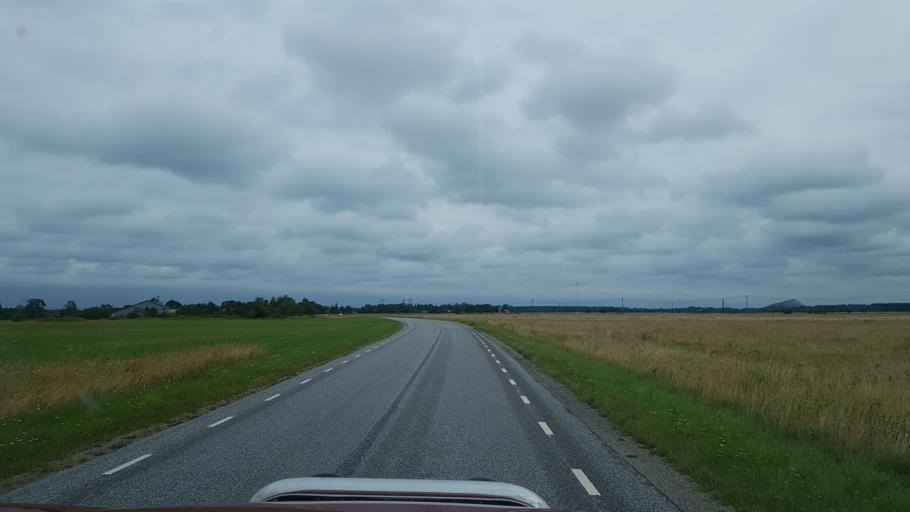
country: EE
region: Ida-Virumaa
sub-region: Puessi linn
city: Pussi
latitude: 59.3924
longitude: 27.0208
